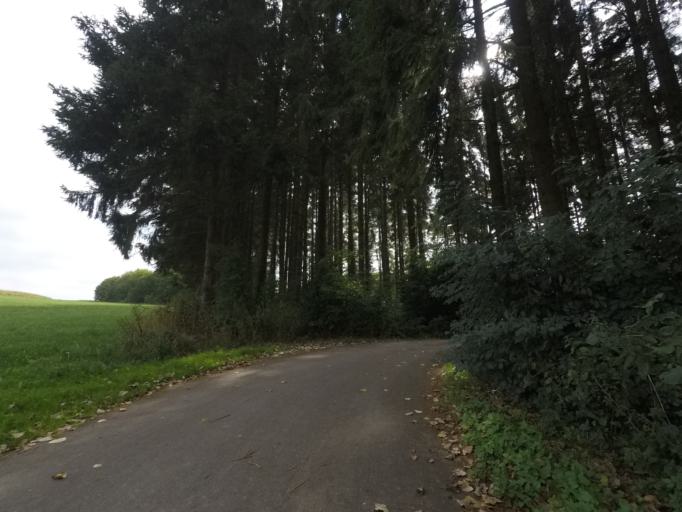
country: BE
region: Wallonia
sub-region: Province du Luxembourg
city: Martelange
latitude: 49.8153
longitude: 5.7512
